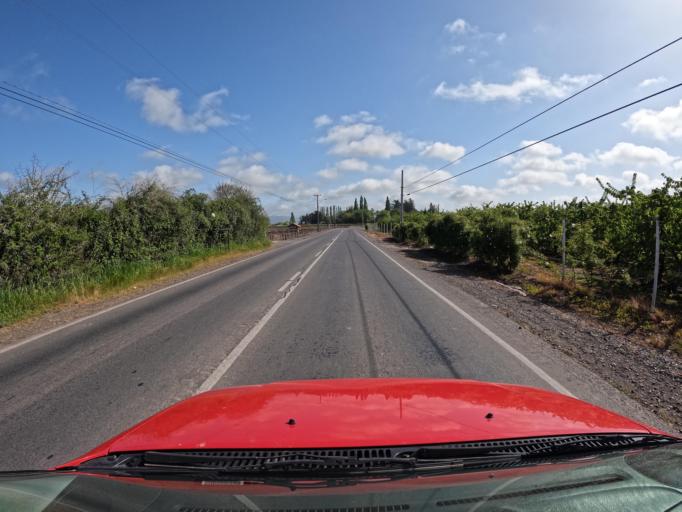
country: CL
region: Maule
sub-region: Provincia de Curico
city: Rauco
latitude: -34.9079
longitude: -71.2787
